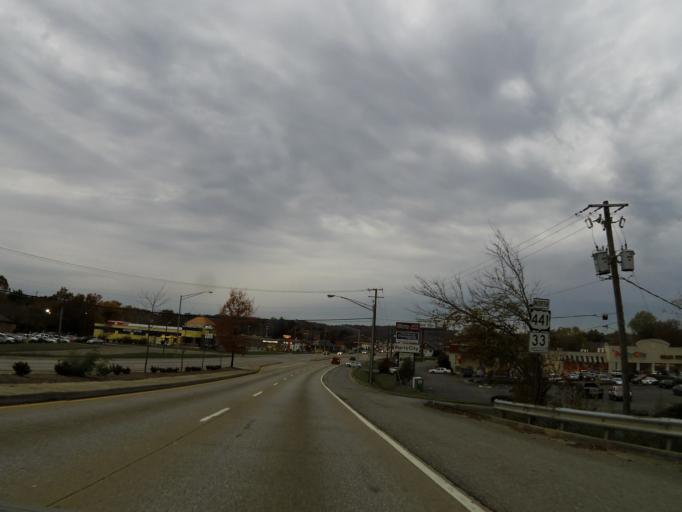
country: US
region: Tennessee
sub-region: Knox County
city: Knoxville
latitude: 36.0225
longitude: -83.9248
